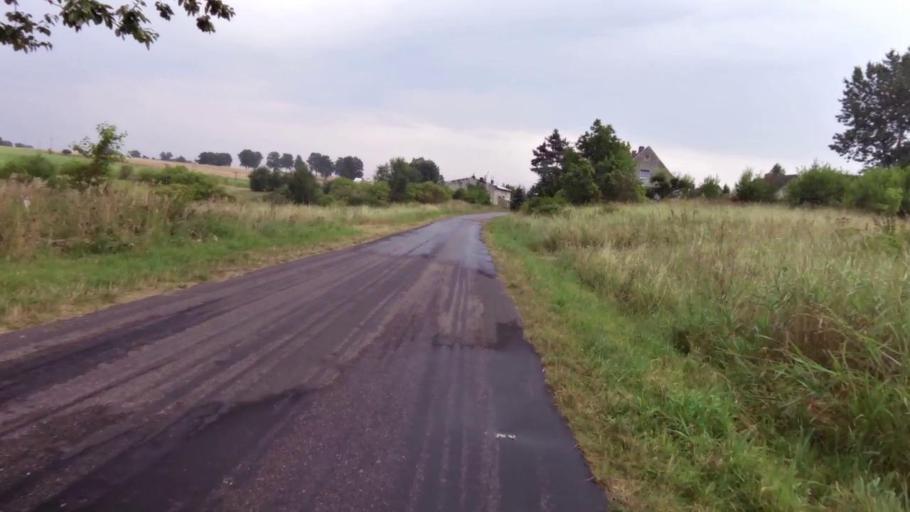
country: PL
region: West Pomeranian Voivodeship
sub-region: Powiat drawski
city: Drawsko Pomorskie
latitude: 53.5305
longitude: 15.7604
